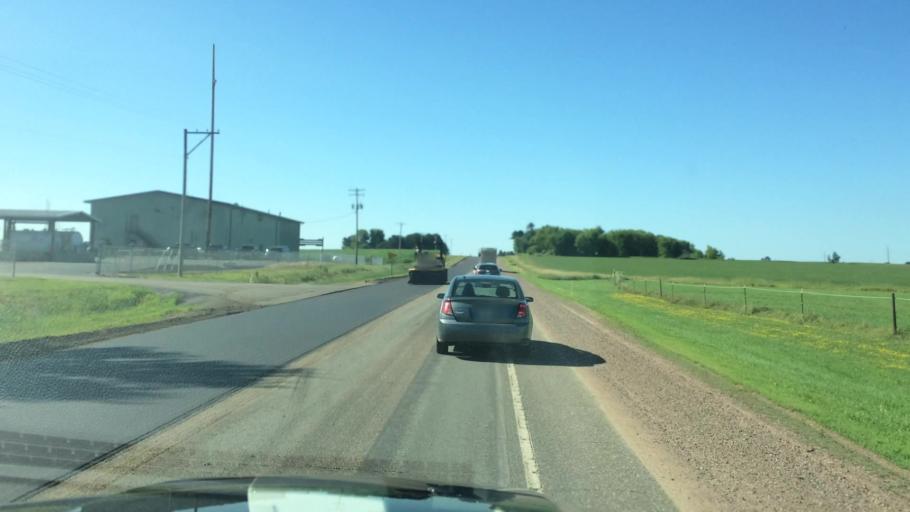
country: US
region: Wisconsin
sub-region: Marathon County
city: Stratford
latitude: 44.8928
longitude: -90.0789
